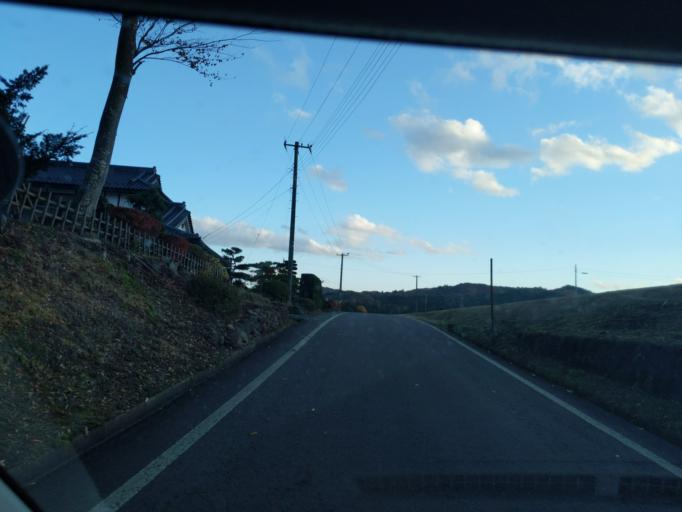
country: JP
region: Iwate
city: Mizusawa
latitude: 39.0397
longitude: 141.0552
